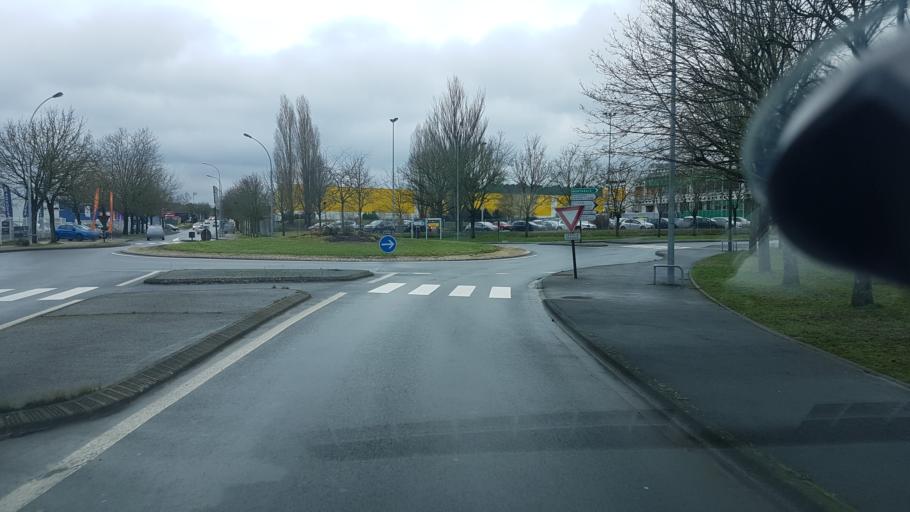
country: FR
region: Ile-de-France
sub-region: Departement de Seine-et-Marne
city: Nemours
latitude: 48.2664
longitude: 2.7147
